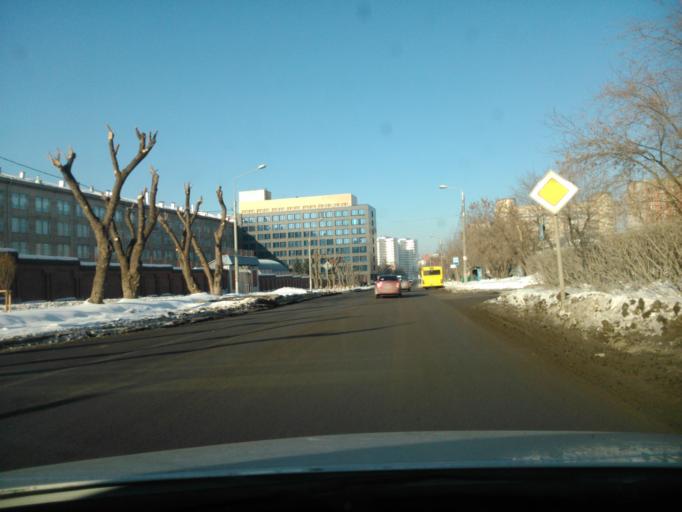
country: RU
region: Perm
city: Perm
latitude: 57.9893
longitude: 56.2010
